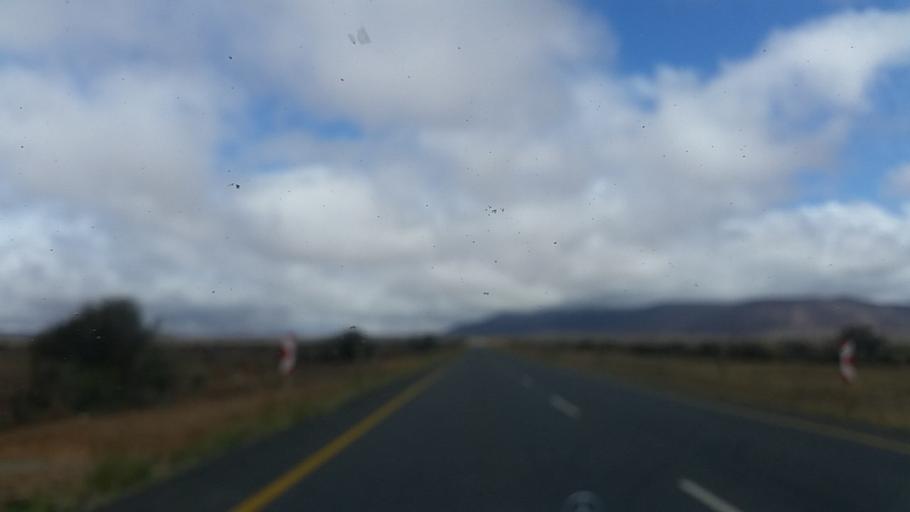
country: ZA
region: Eastern Cape
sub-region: Cacadu District Municipality
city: Graaff-Reinet
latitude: -32.0082
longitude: 24.6561
